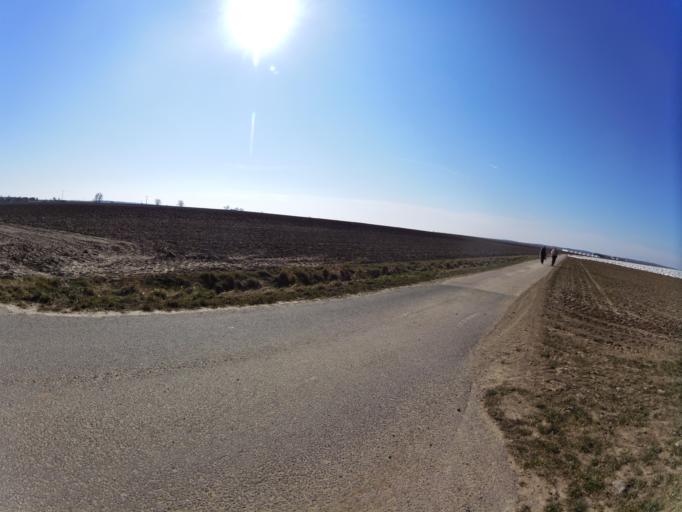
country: DE
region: Bavaria
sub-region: Regierungsbezirk Unterfranken
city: Oberpleichfeld
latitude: 49.8848
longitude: 10.0805
